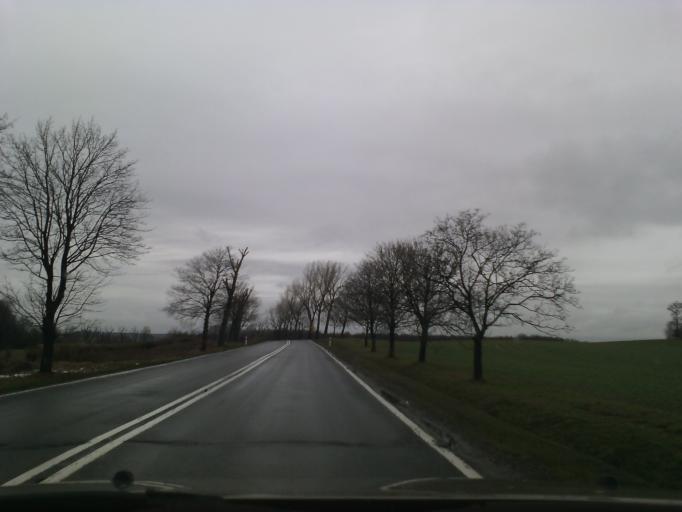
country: PL
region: Lower Silesian Voivodeship
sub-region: Powiat swidnicki
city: Swiebodzice
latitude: 50.8406
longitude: 16.3979
